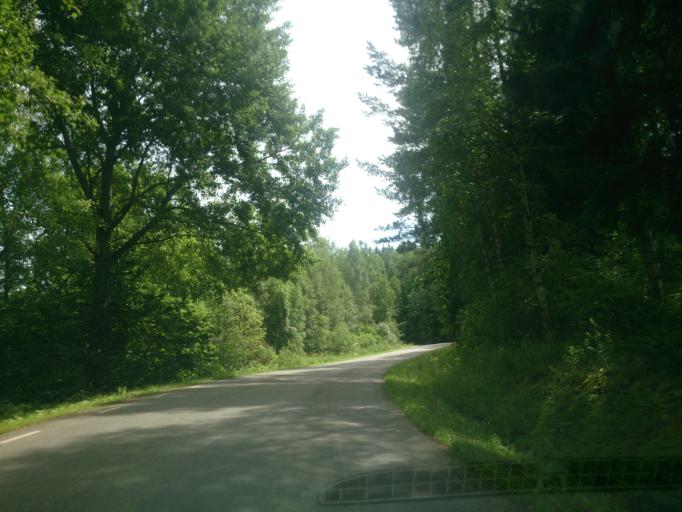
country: SE
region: OEstergoetland
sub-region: Soderkopings Kommun
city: Soederkoeping
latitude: 58.3193
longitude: 16.2872
